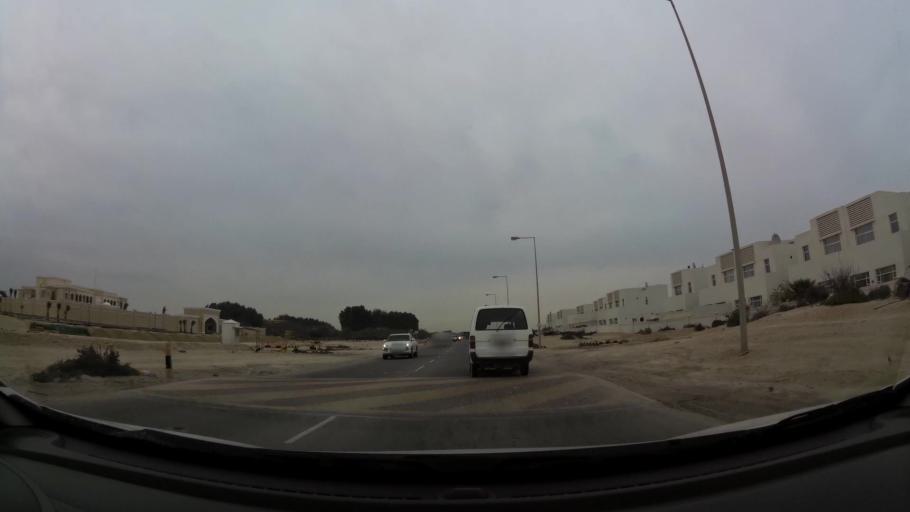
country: BH
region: Northern
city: Ar Rifa'
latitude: 26.0912
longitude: 50.5646
